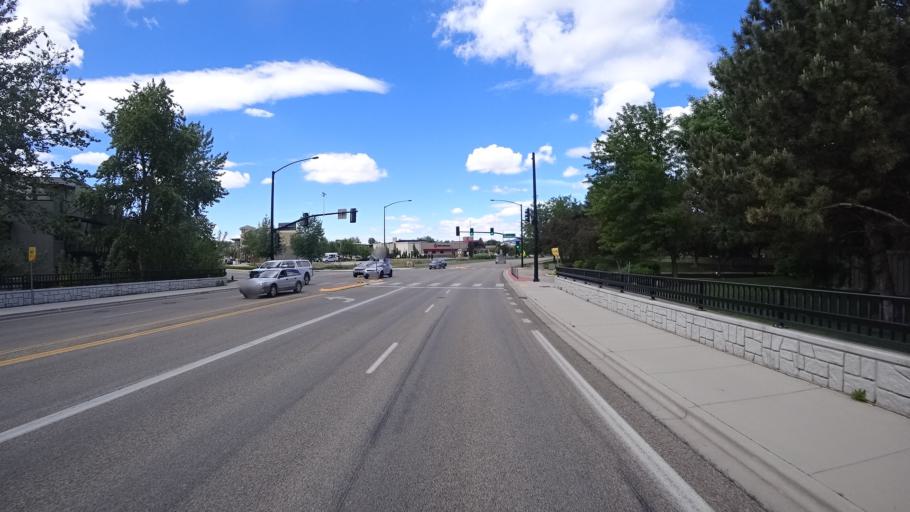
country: US
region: Idaho
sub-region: Ada County
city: Boise
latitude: 43.5755
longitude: -116.1534
